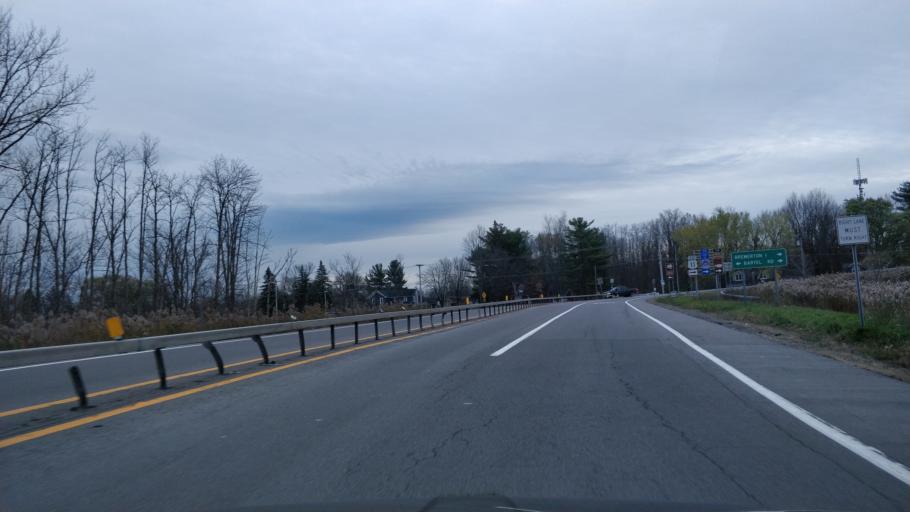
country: US
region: New York
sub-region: Onondaga County
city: Brewerton
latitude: 43.2325
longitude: -76.1271
